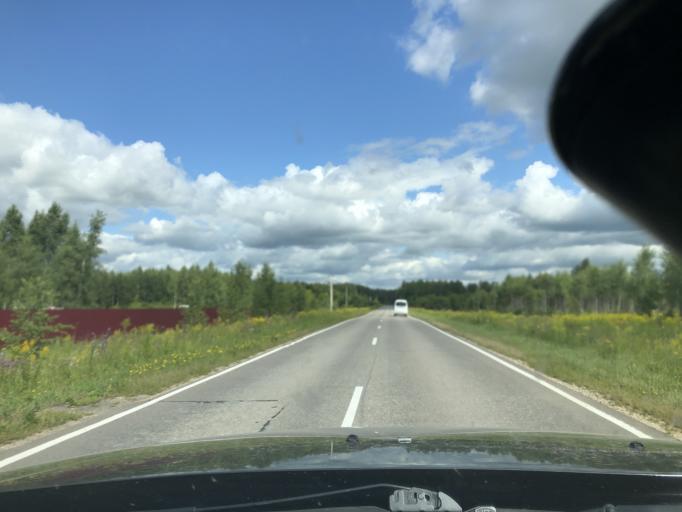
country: RU
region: Tula
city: Revyakino
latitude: 54.4169
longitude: 37.6924
